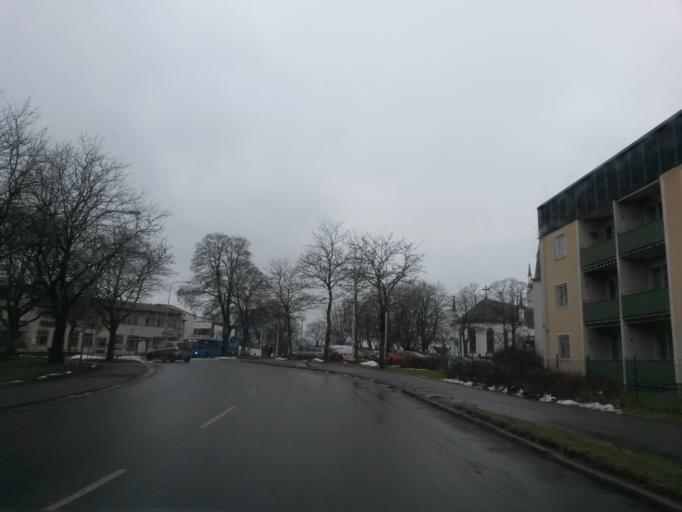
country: SE
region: Vaestra Goetaland
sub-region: Marks Kommun
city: Kinna
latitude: 57.5091
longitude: 12.6982
